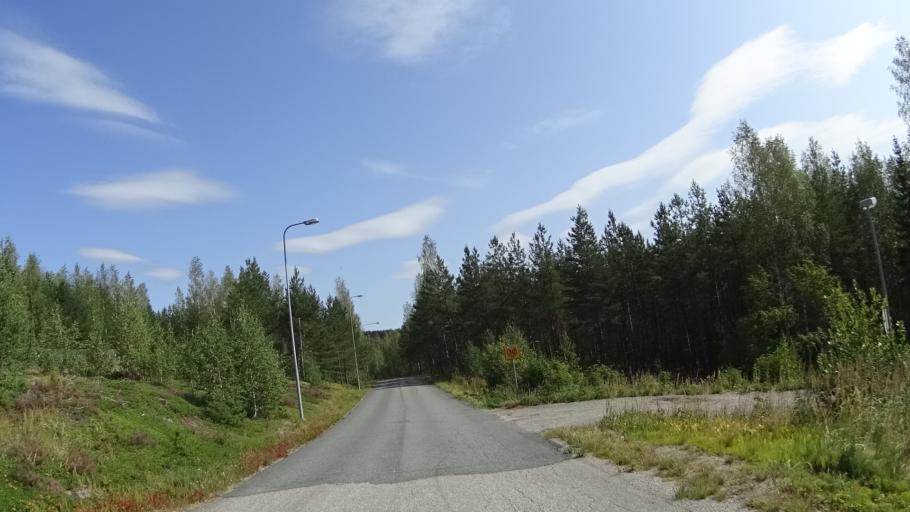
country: FI
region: Pirkanmaa
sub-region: Ylae-Pirkanmaa
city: Maenttae
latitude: 61.8588
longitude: 24.8196
